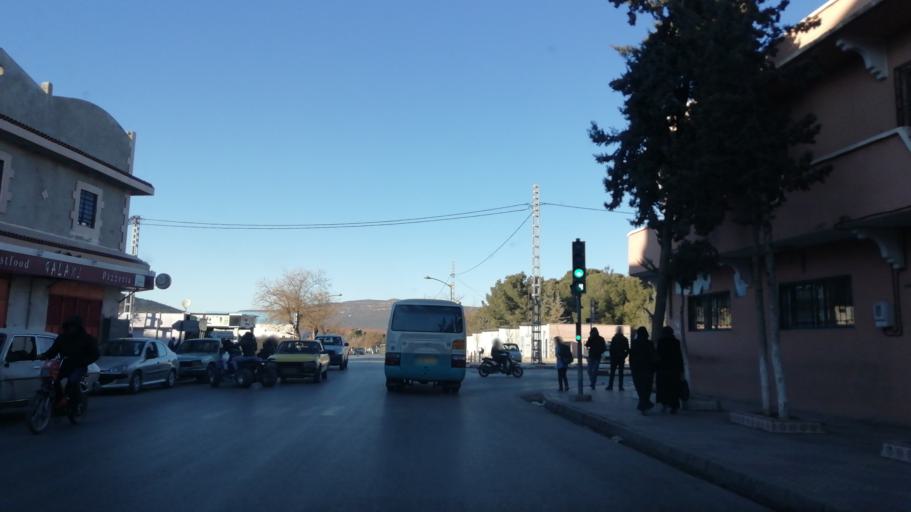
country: DZ
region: Tlemcen
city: Sebdou
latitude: 34.6332
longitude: -1.3330
